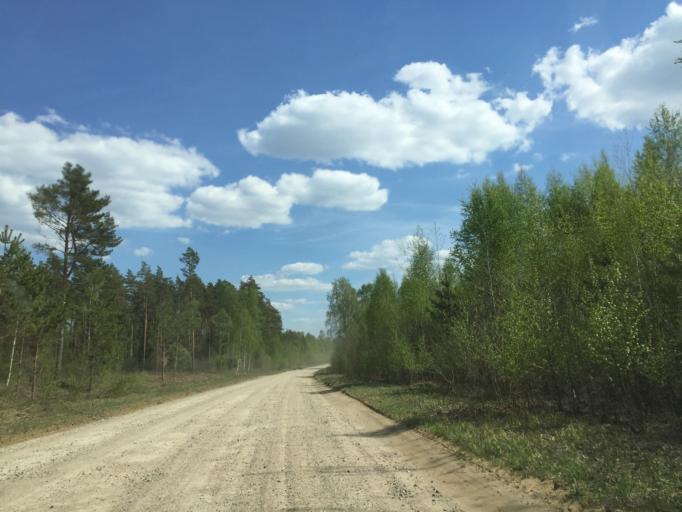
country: LV
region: Limbazu Rajons
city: Limbazi
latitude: 57.3834
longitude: 24.6736
